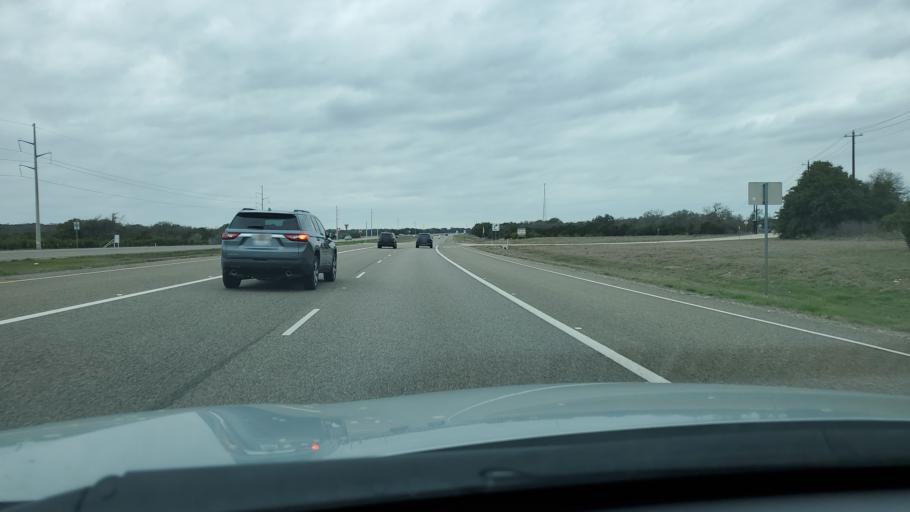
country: US
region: Texas
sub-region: Williamson County
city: Serenada
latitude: 30.7636
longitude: -97.7464
